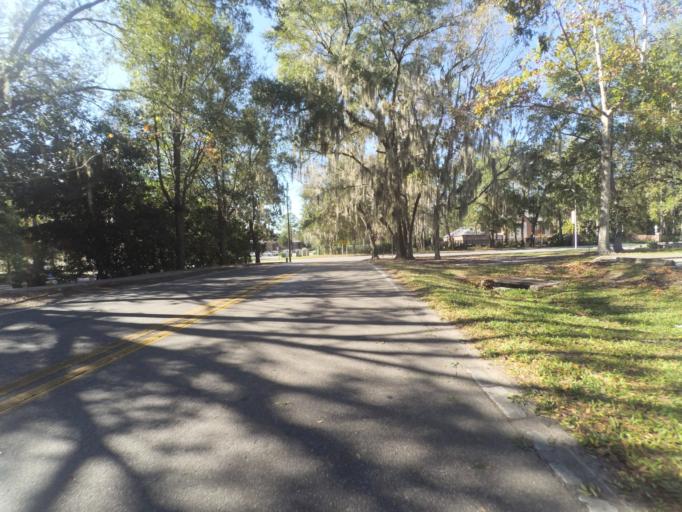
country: US
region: Florida
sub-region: Alachua County
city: Gainesville
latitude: 29.6478
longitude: -82.3594
